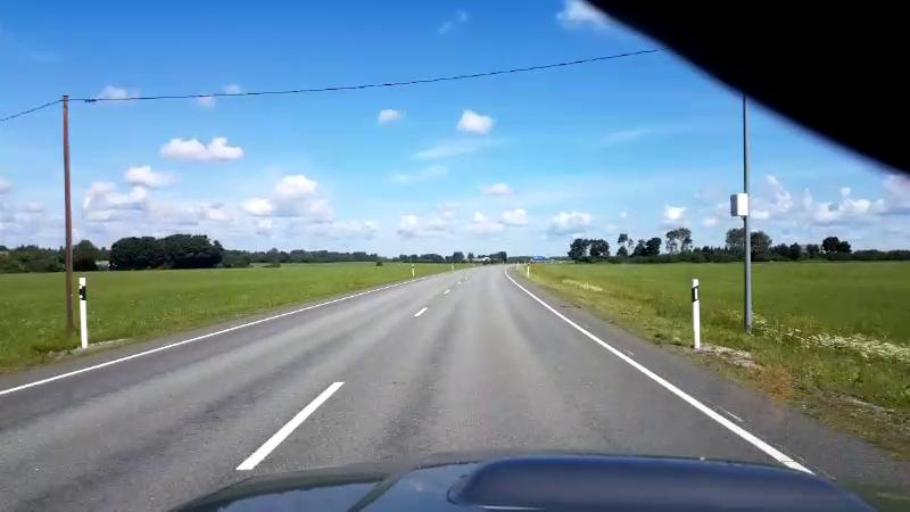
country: EE
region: Jaervamaa
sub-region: Jaerva-Jaani vald
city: Jarva-Jaani
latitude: 59.1661
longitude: 25.7590
